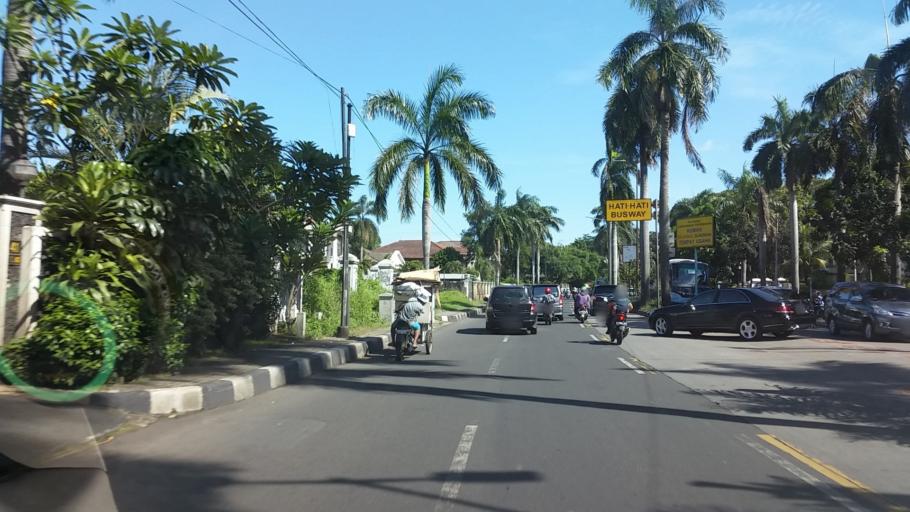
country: ID
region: Banten
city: South Tangerang
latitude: -6.2833
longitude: 106.7801
